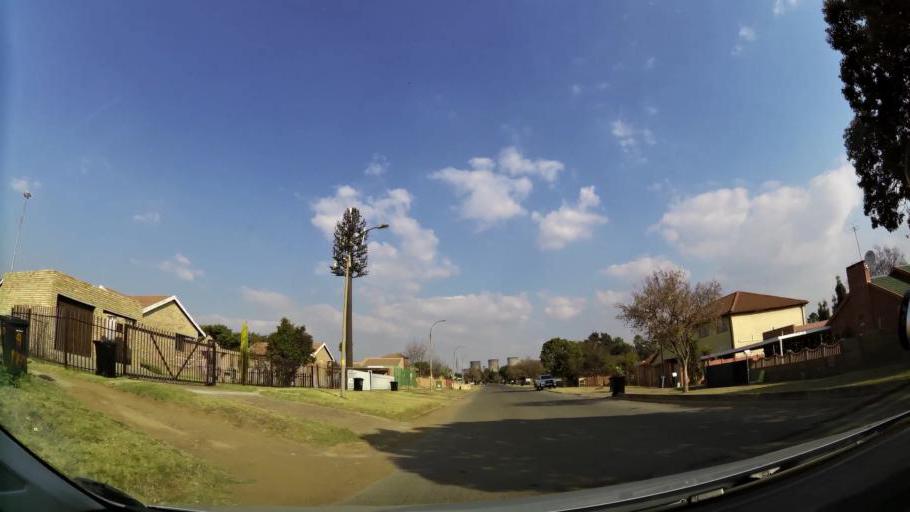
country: ZA
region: Gauteng
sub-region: City of Johannesburg Metropolitan Municipality
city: Modderfontein
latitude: -26.0990
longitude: 28.1924
